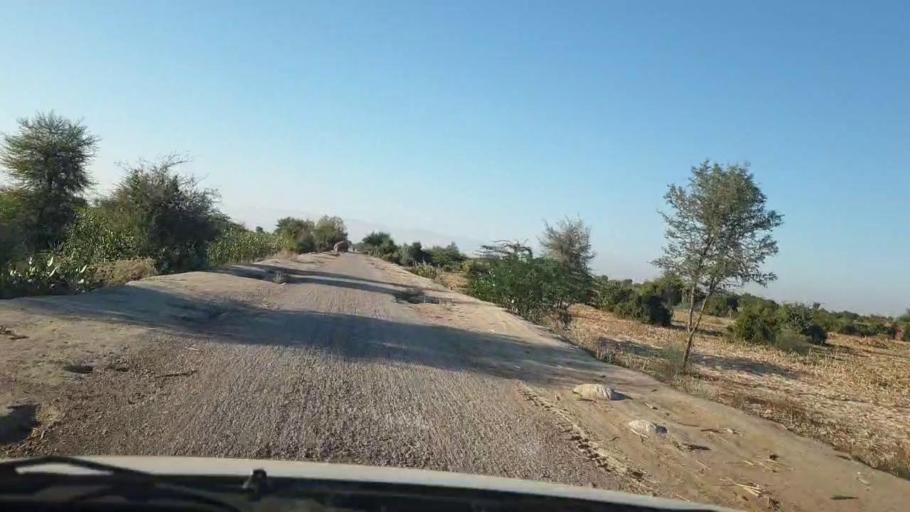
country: PK
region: Sindh
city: Johi
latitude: 26.7686
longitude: 67.4605
